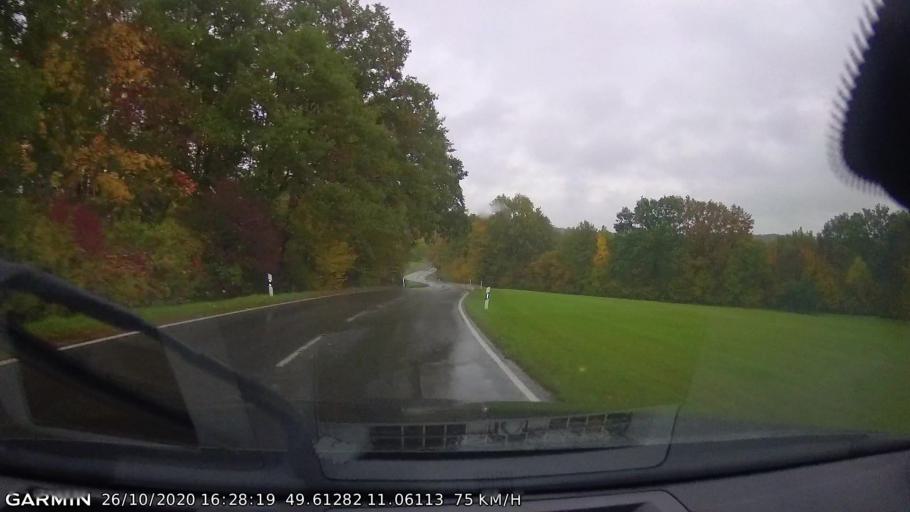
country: DE
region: Bavaria
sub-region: Regierungsbezirk Mittelfranken
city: Marloffstein
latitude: 49.6129
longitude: 11.0614
